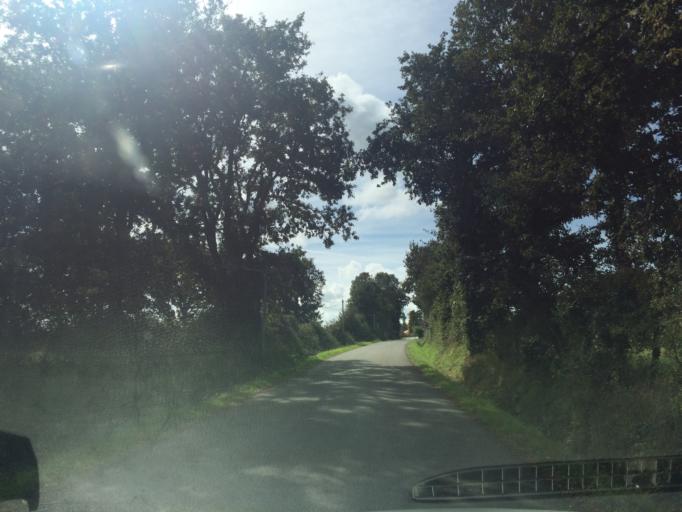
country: FR
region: Pays de la Loire
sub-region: Departement de la Loire-Atlantique
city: Chemere
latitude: 47.1119
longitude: -1.9172
